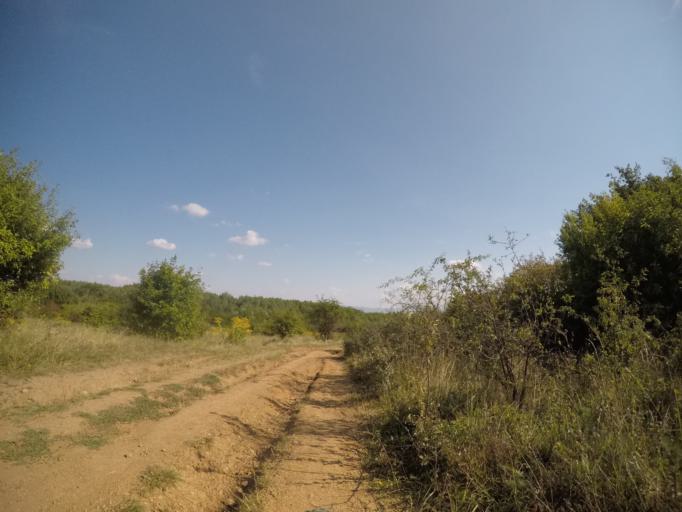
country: SK
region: Kosicky
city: Kosice
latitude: 48.7384
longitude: 21.2101
